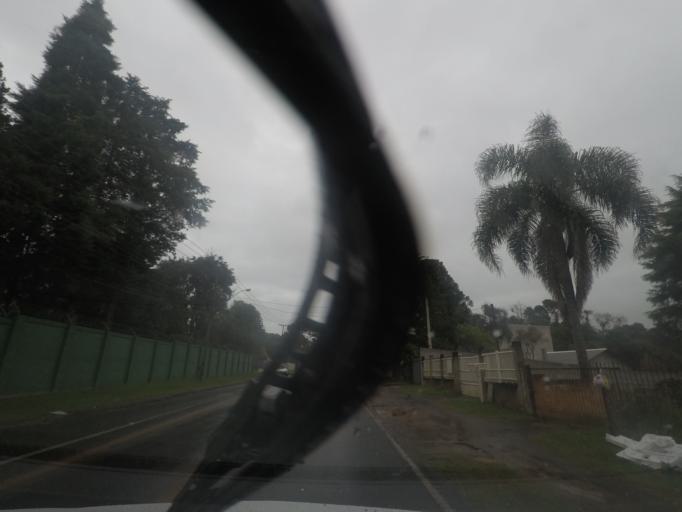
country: BR
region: Parana
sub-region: Quatro Barras
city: Quatro Barras
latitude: -25.3742
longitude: -49.1017
